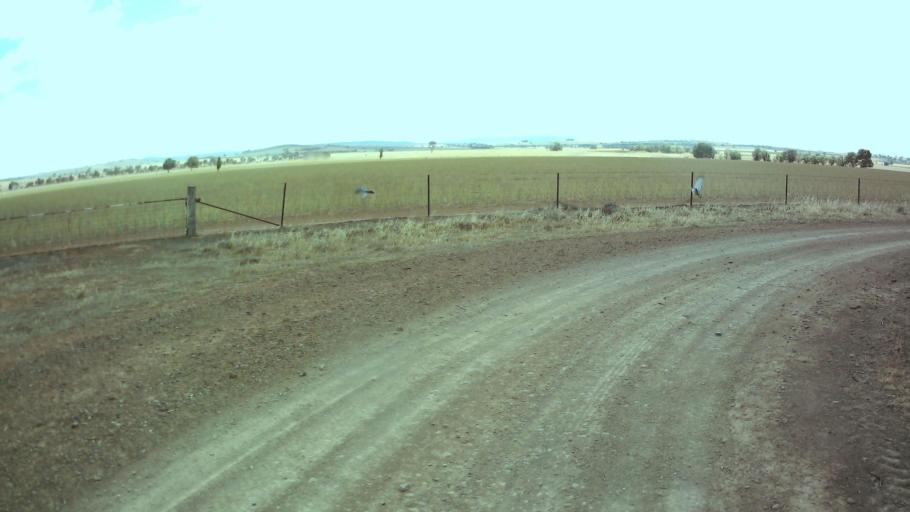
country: AU
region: New South Wales
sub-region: Weddin
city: Grenfell
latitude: -33.9955
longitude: 148.3022
